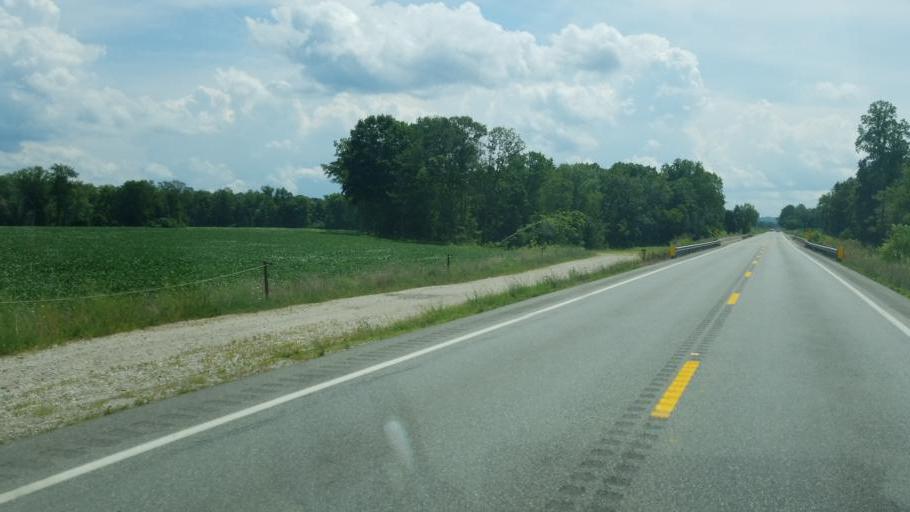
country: US
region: West Virginia
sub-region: Putnam County
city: Buffalo
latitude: 38.6919
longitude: -81.9654
